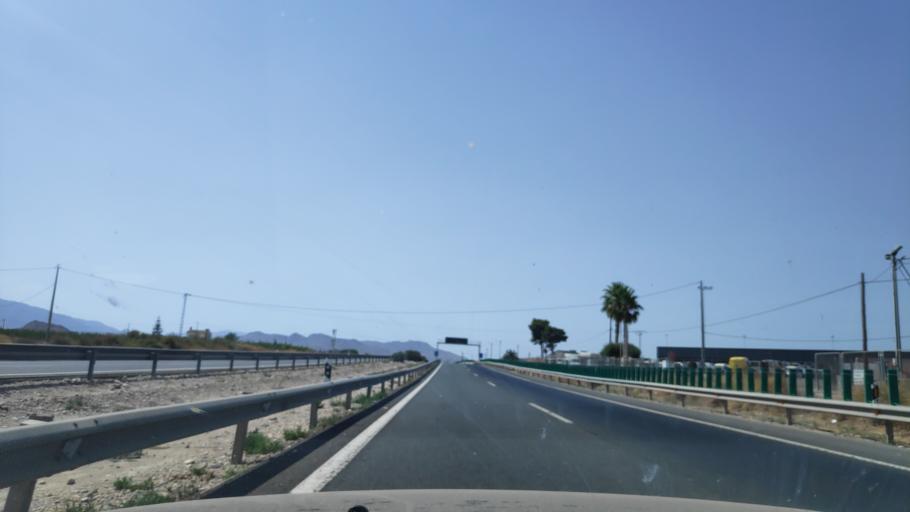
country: ES
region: Murcia
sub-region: Murcia
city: Lorqui
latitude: 38.1178
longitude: -1.2441
